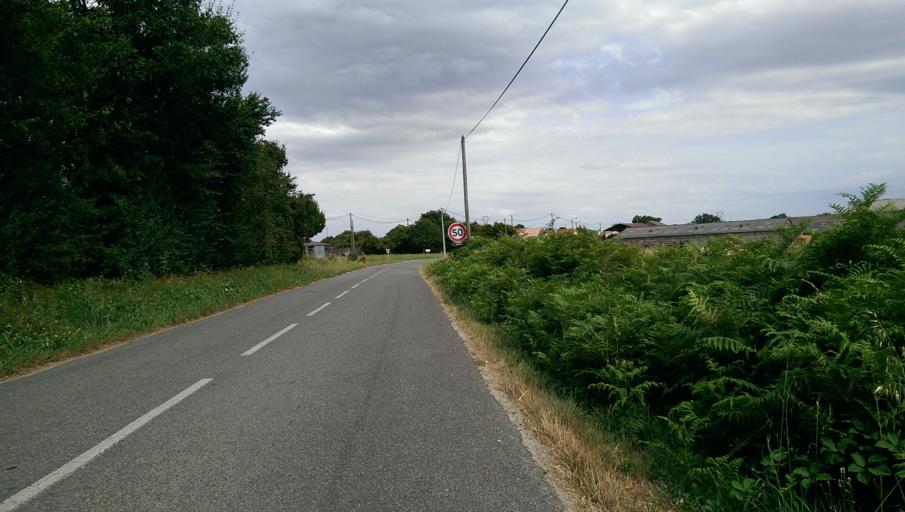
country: FR
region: Pays de la Loire
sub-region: Departement de la Loire-Atlantique
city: La Planche
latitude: 47.0079
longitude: -1.4223
